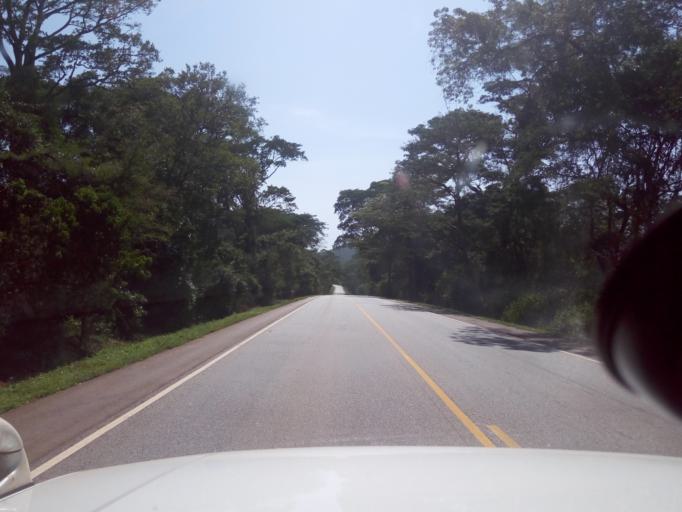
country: UG
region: Eastern Region
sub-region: Busia District
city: Busia
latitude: 0.5367
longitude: 34.0010
